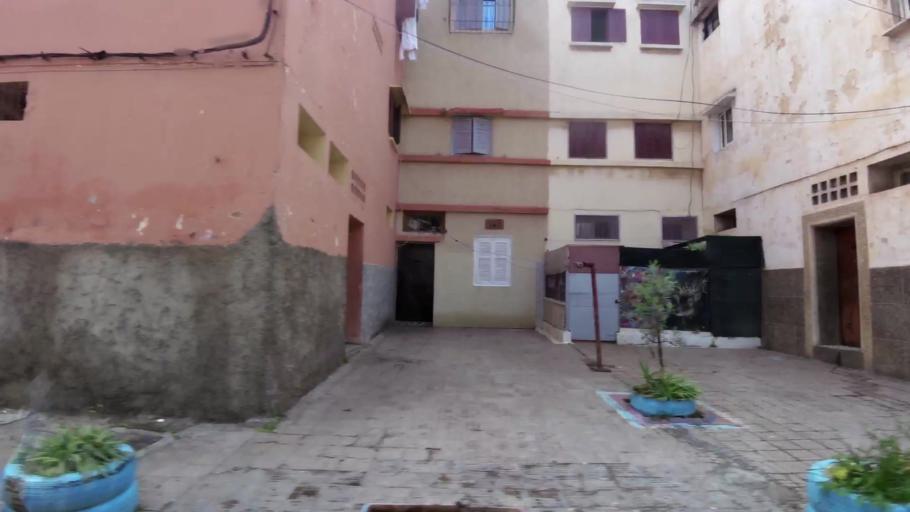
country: MA
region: Grand Casablanca
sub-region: Casablanca
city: Casablanca
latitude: 33.5733
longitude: -7.6807
